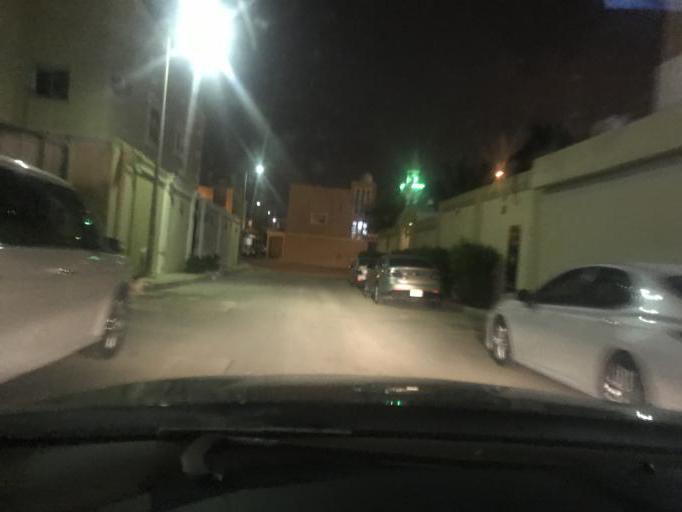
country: SA
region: Ar Riyad
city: Riyadh
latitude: 24.7509
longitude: 46.7523
